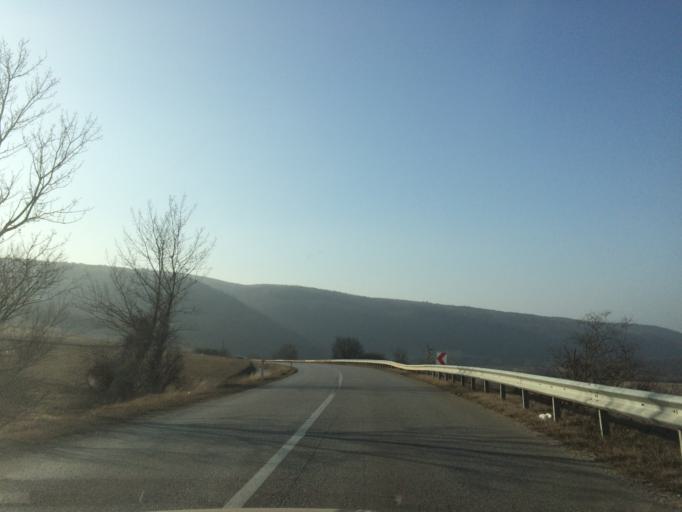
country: XK
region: Pec
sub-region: Komuna e Pejes
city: Kosuriq
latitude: 42.5124
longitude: 20.5475
